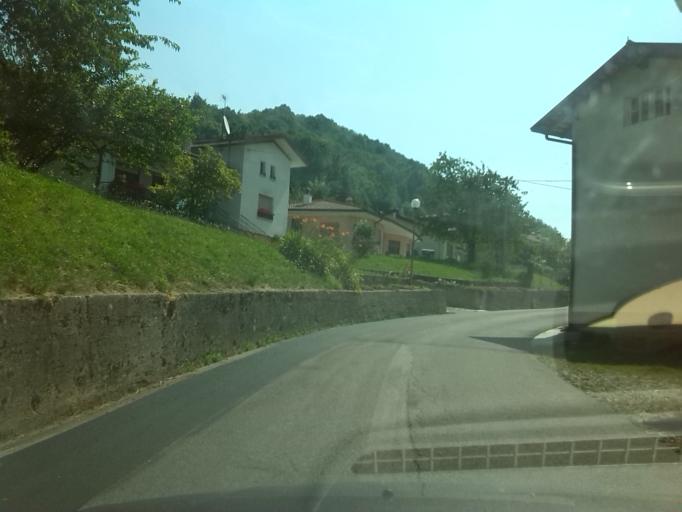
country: IT
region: Friuli Venezia Giulia
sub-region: Provincia di Udine
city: Stregna
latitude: 46.1273
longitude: 13.5763
